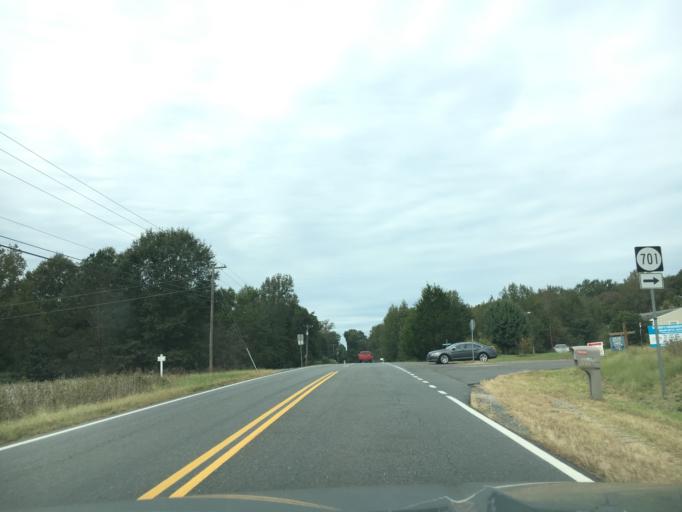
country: US
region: Virginia
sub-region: Goochland County
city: Goochland
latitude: 37.7523
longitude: -77.8623
